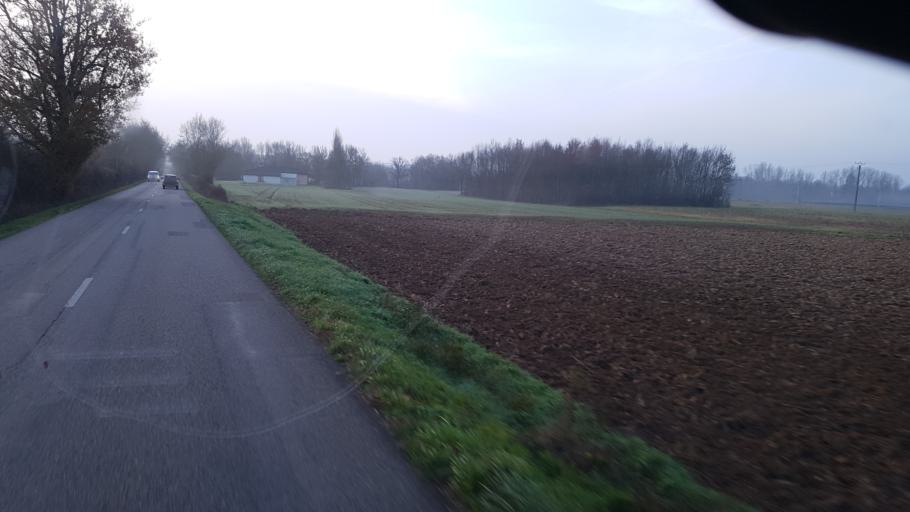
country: FR
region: Midi-Pyrenees
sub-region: Departement du Tarn-et-Garonne
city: Montricoux
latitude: 44.1070
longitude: 1.5968
